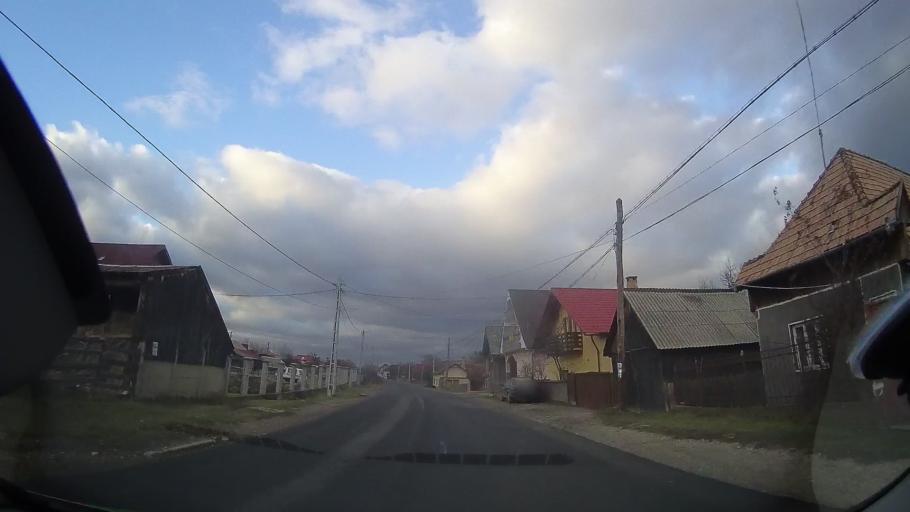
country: RO
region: Cluj
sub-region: Comuna Calatele
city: Calatele
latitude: 46.7721
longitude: 23.0079
